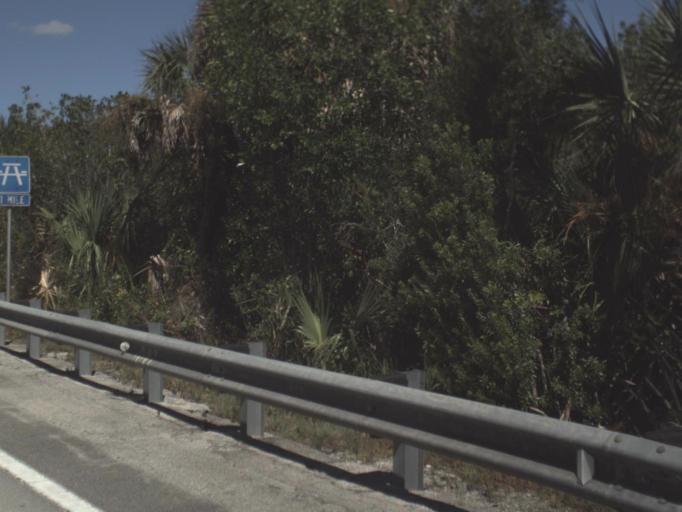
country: US
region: Florida
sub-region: Collier County
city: Marco
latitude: 25.9815
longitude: -81.5626
